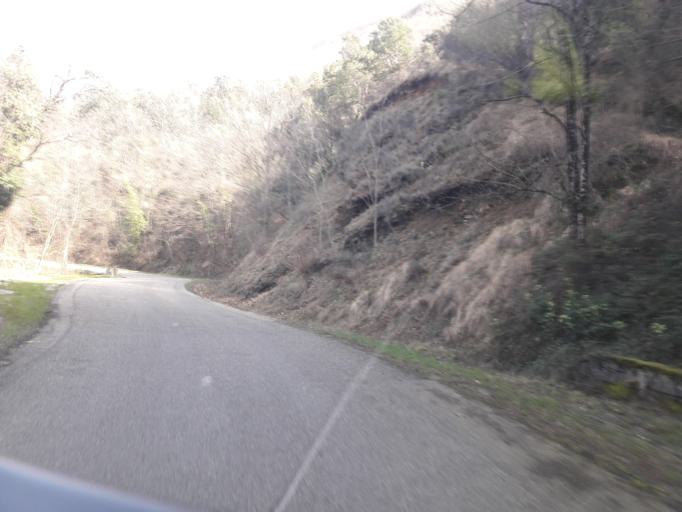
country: FR
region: Languedoc-Roussillon
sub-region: Departement du Gard
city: Sumene
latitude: 43.9906
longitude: 3.7569
